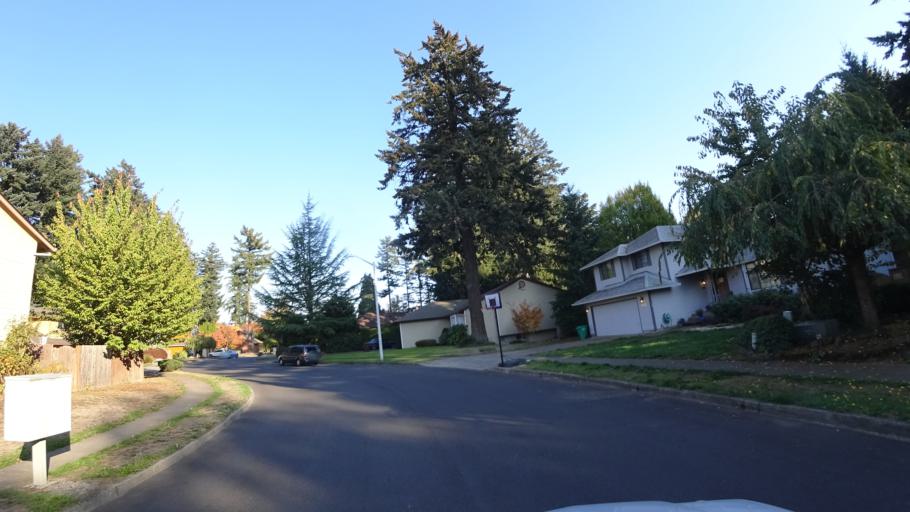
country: US
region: Oregon
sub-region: Multnomah County
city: Gresham
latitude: 45.5076
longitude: -122.4468
